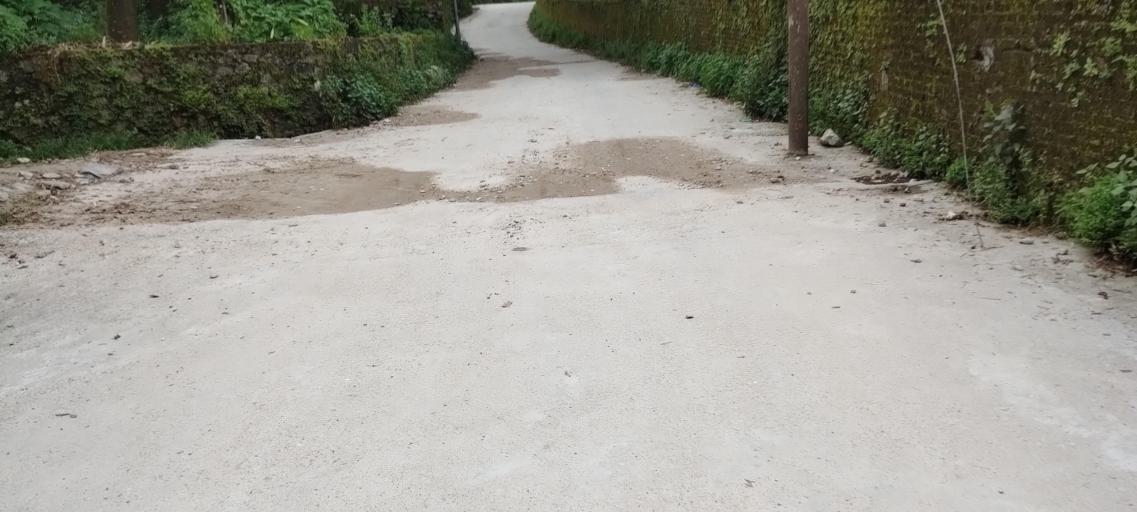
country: NP
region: Central Region
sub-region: Bagmati Zone
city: Kathmandu
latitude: 27.7837
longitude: 85.3617
